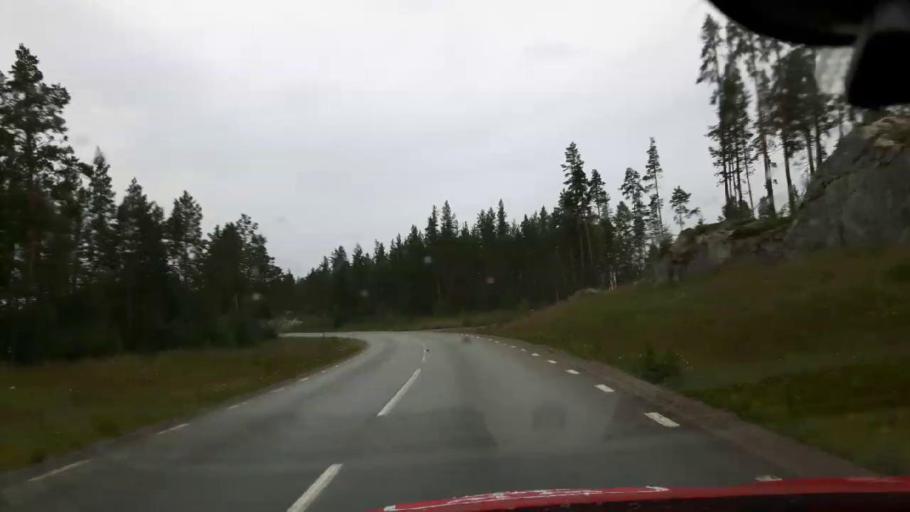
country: SE
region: Jaemtland
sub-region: OEstersunds Kommun
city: Brunflo
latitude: 62.8067
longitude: 14.9972
